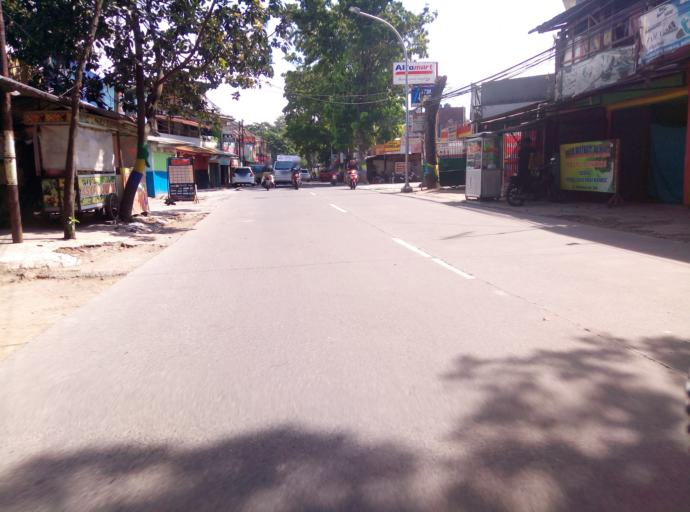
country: ID
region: West Java
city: Bandung
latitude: -6.8851
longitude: 107.6185
